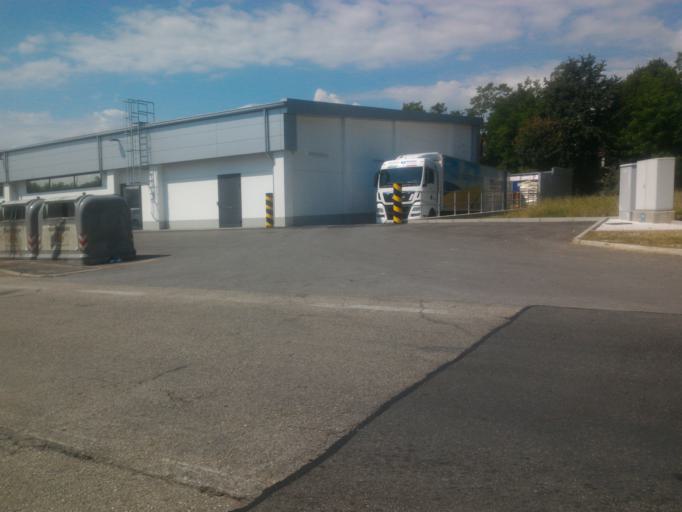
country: IT
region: Piedmont
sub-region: Provincia di Torino
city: Pinerolo
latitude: 44.8894
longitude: 7.3545
